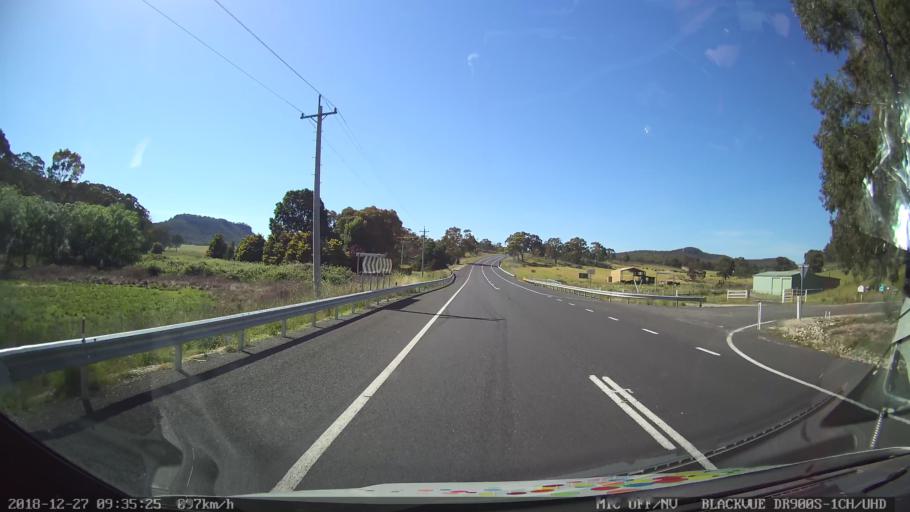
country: AU
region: New South Wales
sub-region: Lithgow
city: Portland
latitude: -33.2384
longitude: 150.0304
